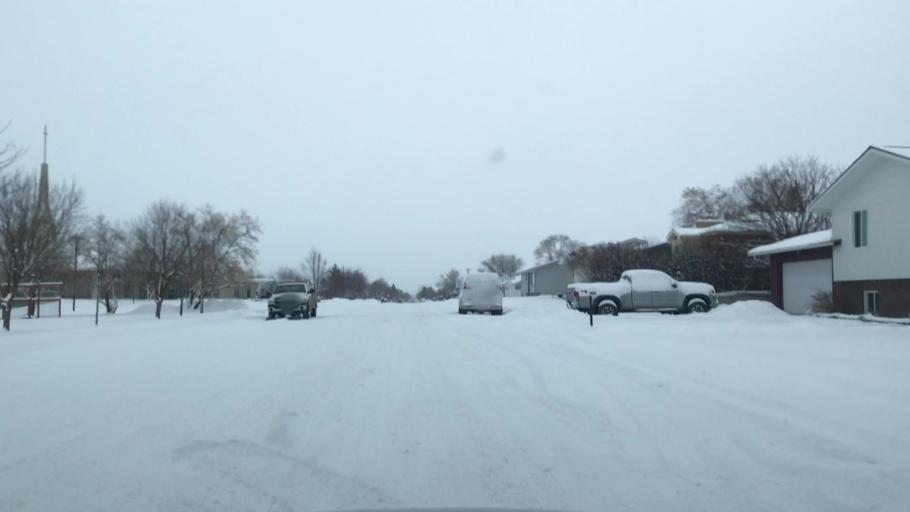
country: US
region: Montana
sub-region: Lewis and Clark County
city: Helena
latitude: 46.5932
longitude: -112.0128
